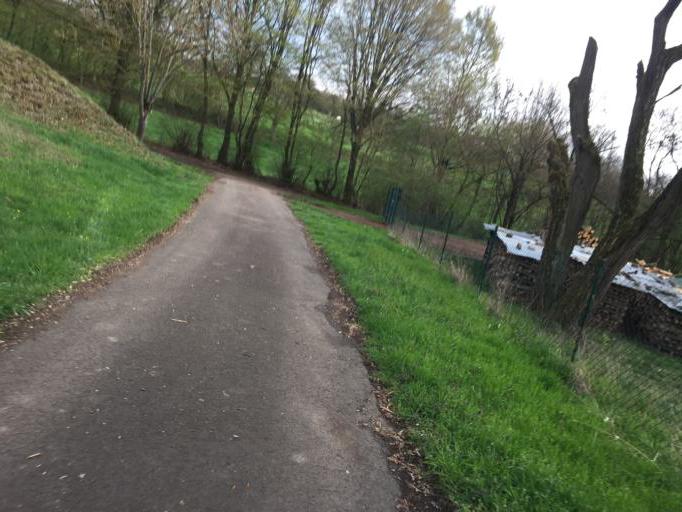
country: DE
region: Hesse
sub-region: Regierungsbezirk Giessen
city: Grunberg
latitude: 50.5839
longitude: 8.9682
